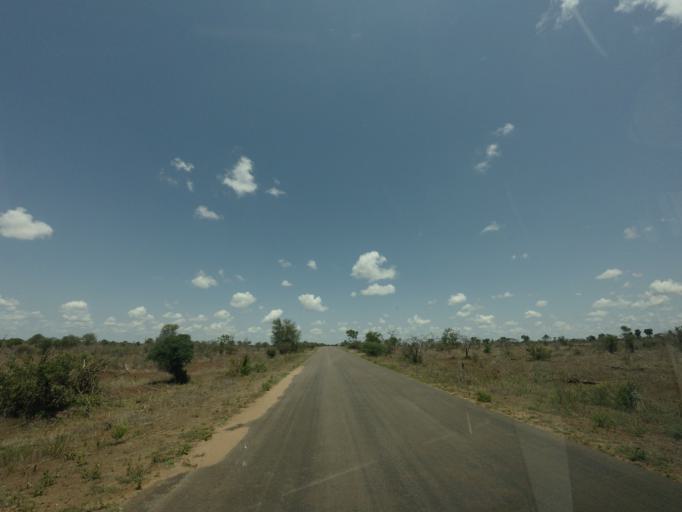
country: ZA
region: Mpumalanga
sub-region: Ehlanzeni District
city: Komatipoort
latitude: -24.8021
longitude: 31.8786
